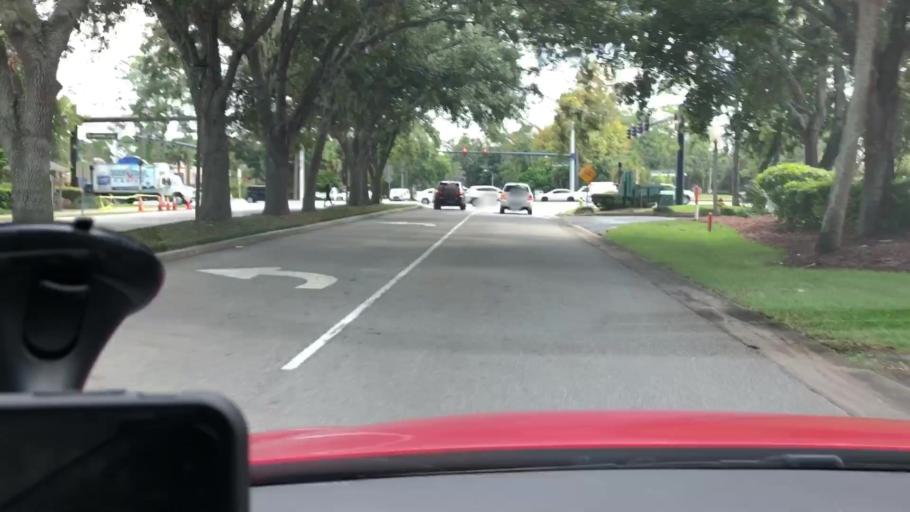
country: US
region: Florida
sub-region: Volusia County
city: Port Orange
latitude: 29.1241
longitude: -81.0127
